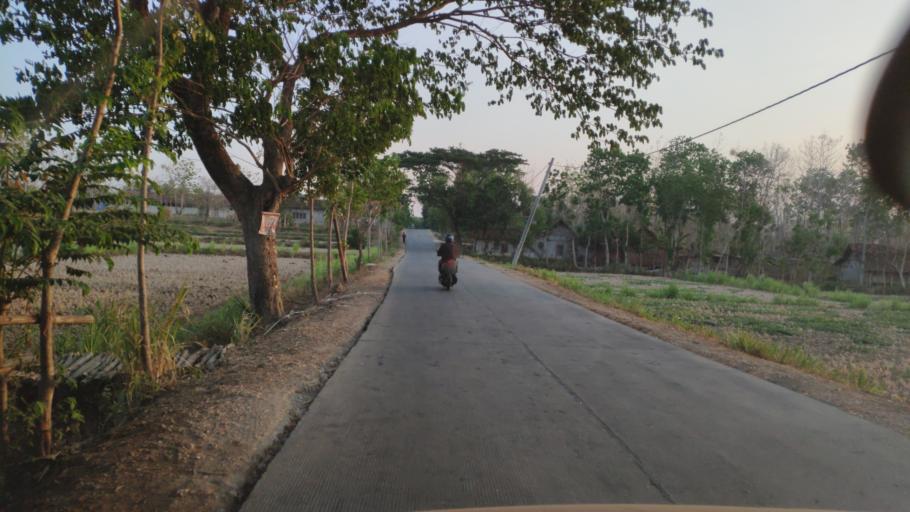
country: ID
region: Central Java
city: Klopoduwur
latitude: -7.0225
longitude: 111.4105
